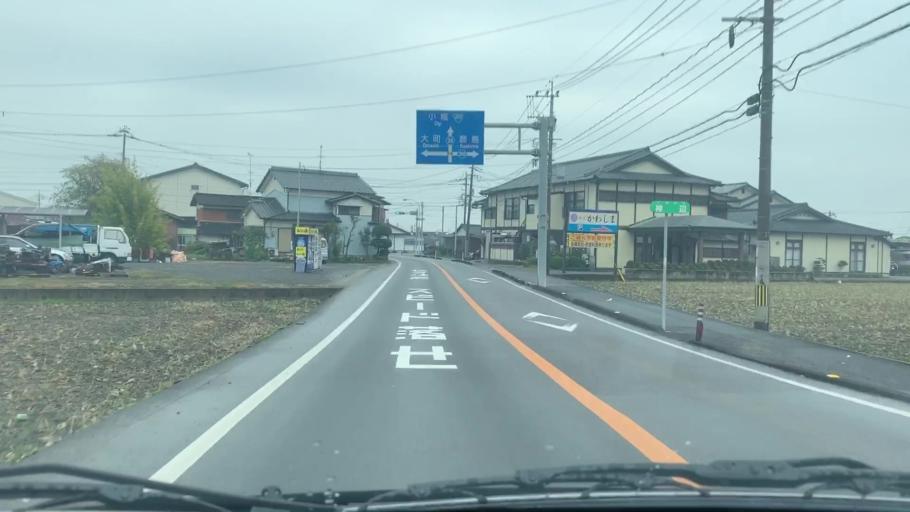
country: JP
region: Saga Prefecture
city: Kashima
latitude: 33.1952
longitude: 130.1131
